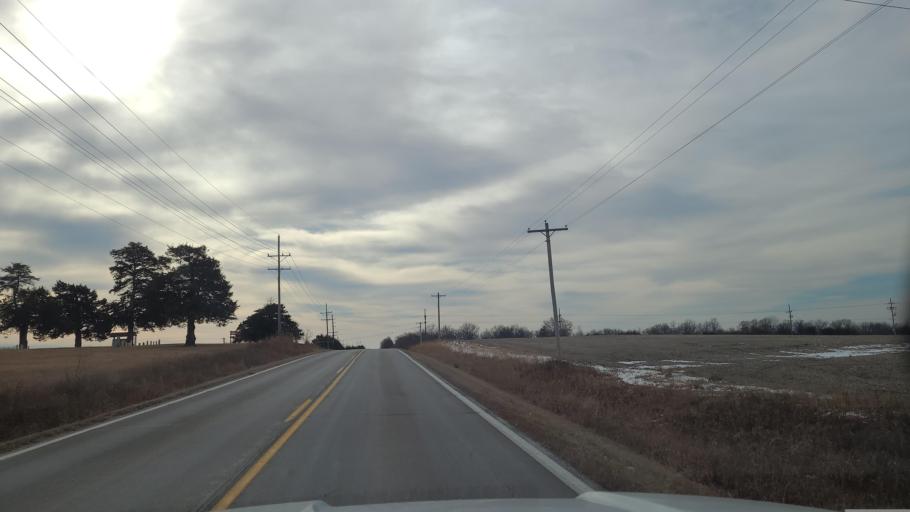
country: US
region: Kansas
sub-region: Douglas County
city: Baldwin City
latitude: 38.7624
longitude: -95.1865
